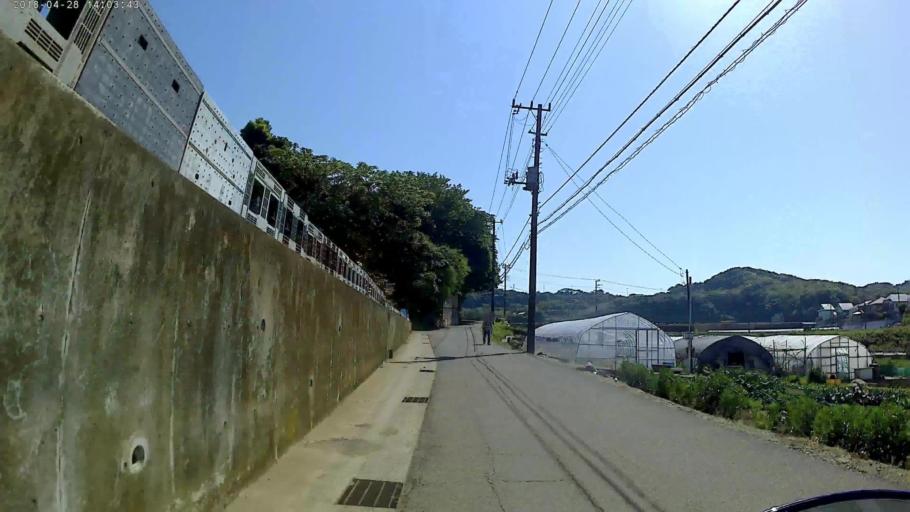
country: JP
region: Kanagawa
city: Miura
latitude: 35.1605
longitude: 139.6581
